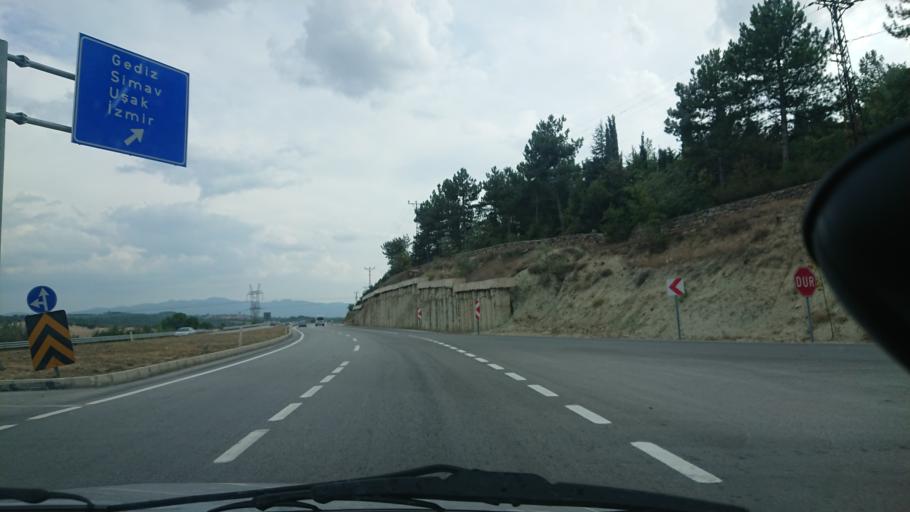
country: TR
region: Kuetahya
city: Gediz
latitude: 39.0312
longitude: 29.4162
